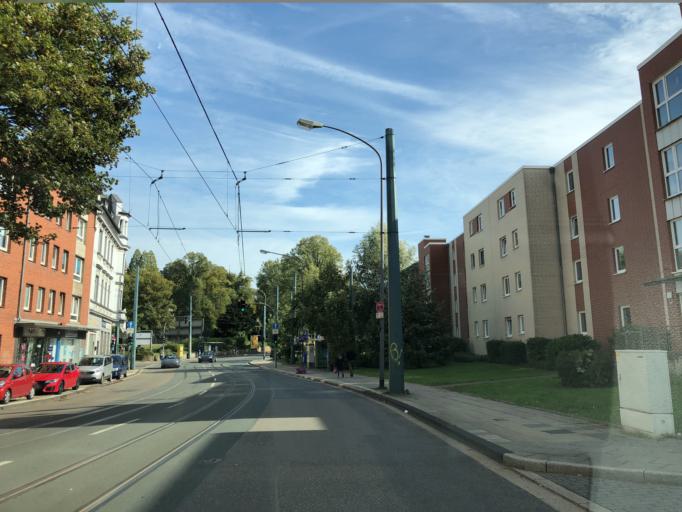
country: DE
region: North Rhine-Westphalia
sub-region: Regierungsbezirk Dusseldorf
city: Essen
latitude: 51.4733
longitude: 7.0327
